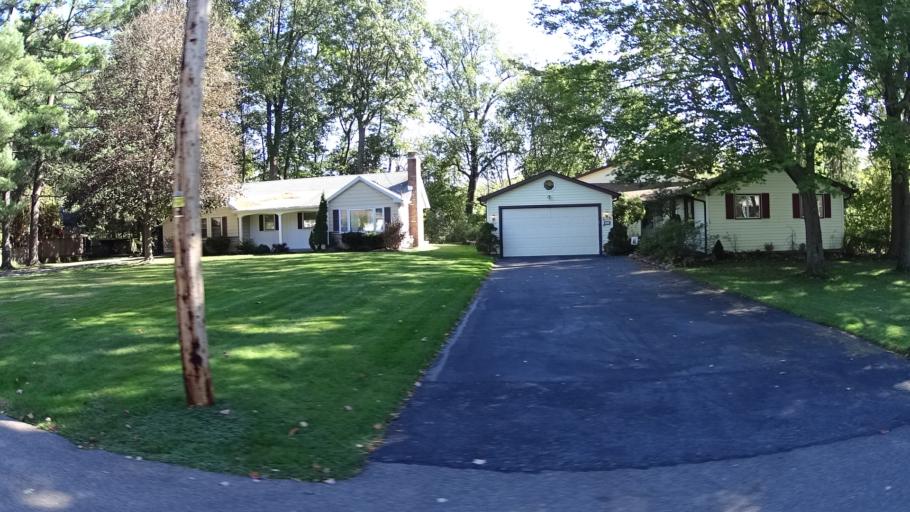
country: US
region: Ohio
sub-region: Lorain County
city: Amherst
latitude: 41.3958
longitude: -82.2343
